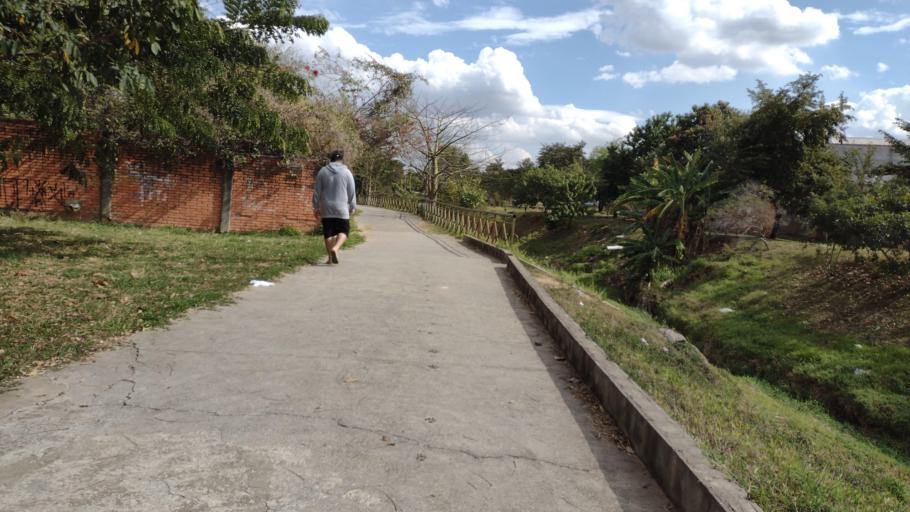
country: BR
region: Sao Paulo
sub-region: Sorocaba
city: Sorocaba
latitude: -23.4588
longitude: -47.4696
